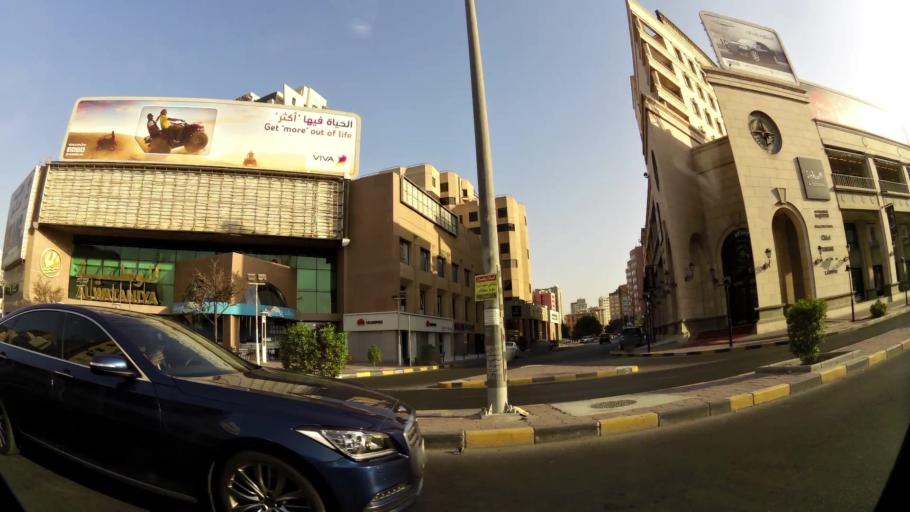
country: KW
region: Muhafazat Hawalli
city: As Salimiyah
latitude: 29.3406
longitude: 48.0707
